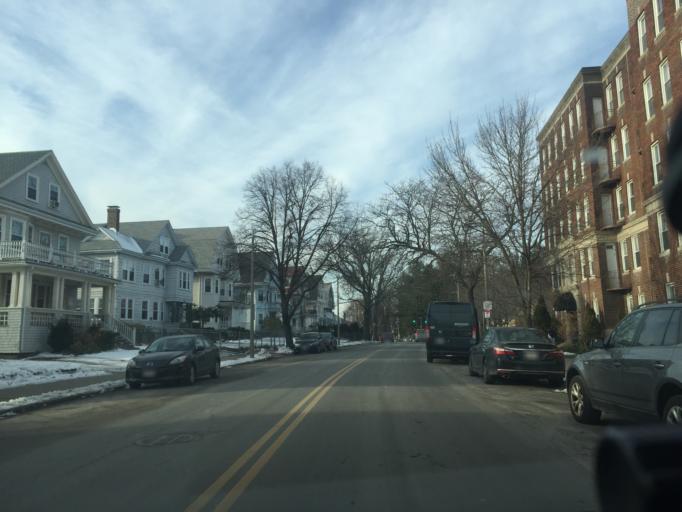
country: US
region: Massachusetts
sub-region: Norfolk County
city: Brookline
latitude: 42.3450
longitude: -71.1451
